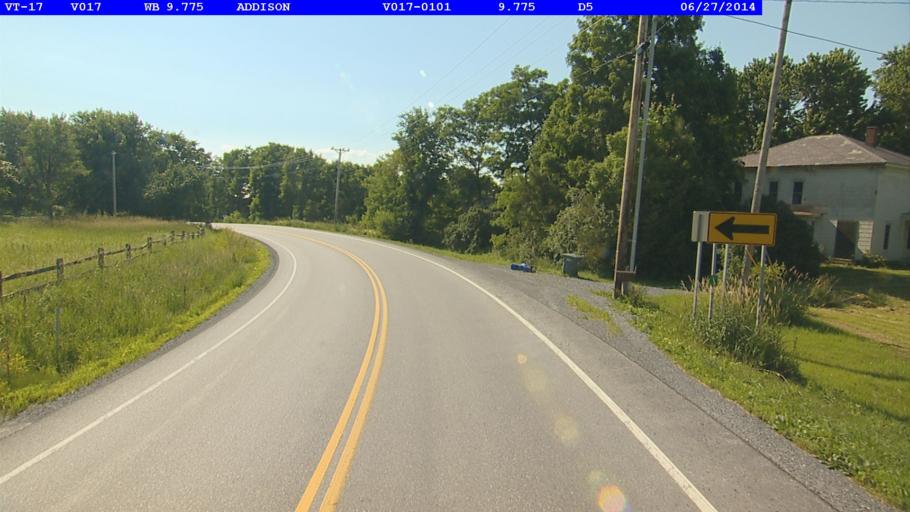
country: US
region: Vermont
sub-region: Addison County
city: Vergennes
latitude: 44.0854
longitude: -73.2758
